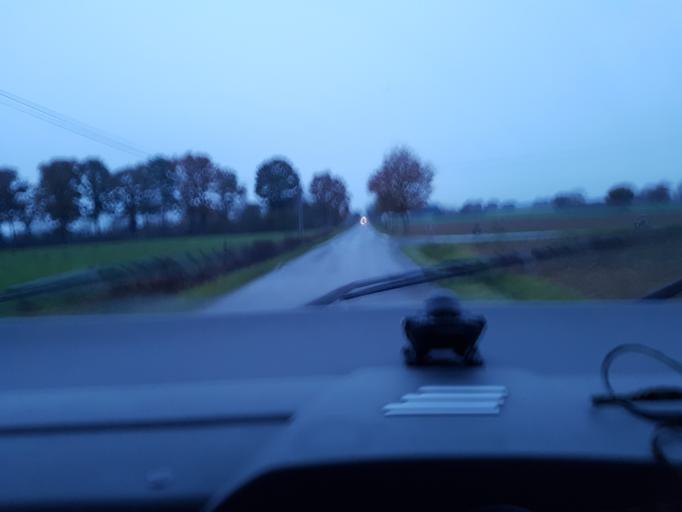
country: FR
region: Brittany
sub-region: Departement d'Ille-et-Vilaine
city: Montreuil-sous-Perouse
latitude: 48.2015
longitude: -1.2625
